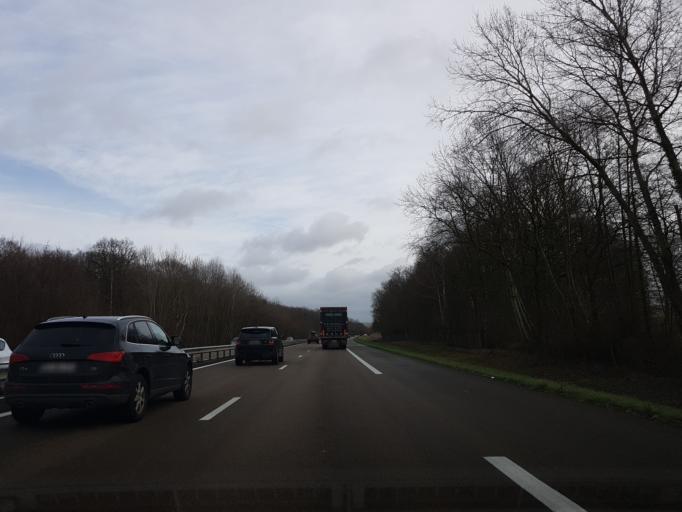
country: FR
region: Champagne-Ardenne
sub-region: Departement de l'Aube
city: Bar-sur-Seine
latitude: 48.1831
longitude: 4.3998
